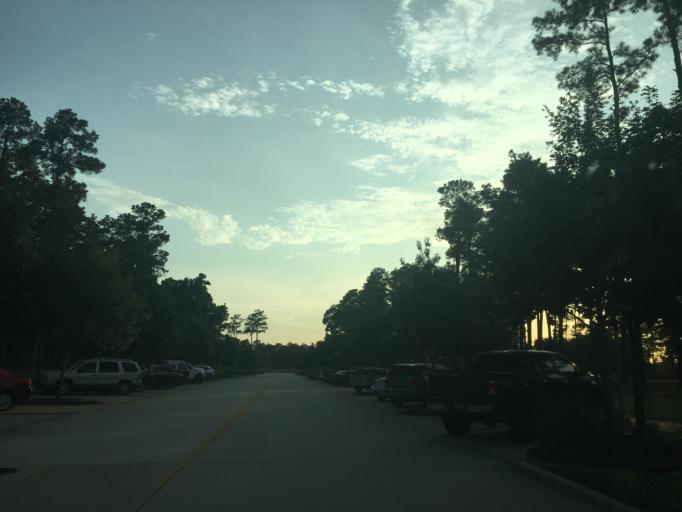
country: US
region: Texas
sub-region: Harris County
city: Spring
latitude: 30.0980
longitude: -95.4428
